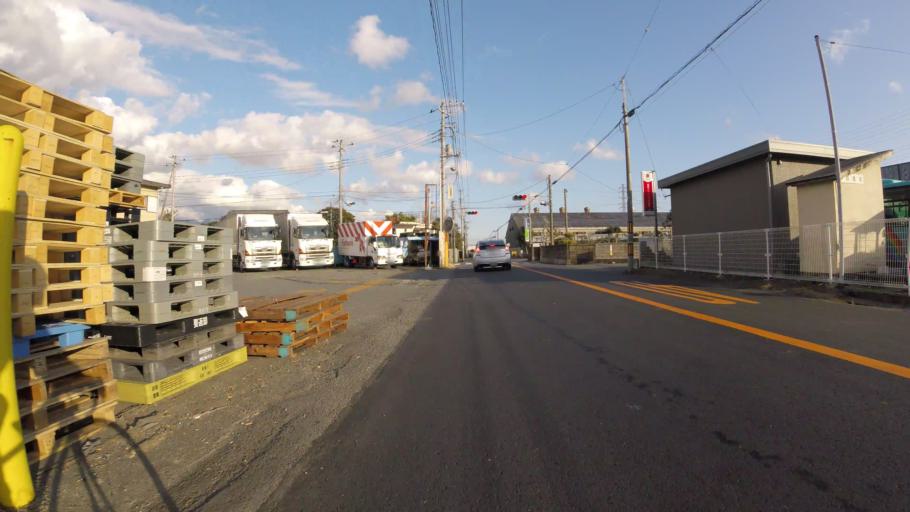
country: JP
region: Shizuoka
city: Fuji
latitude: 35.1519
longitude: 138.6662
